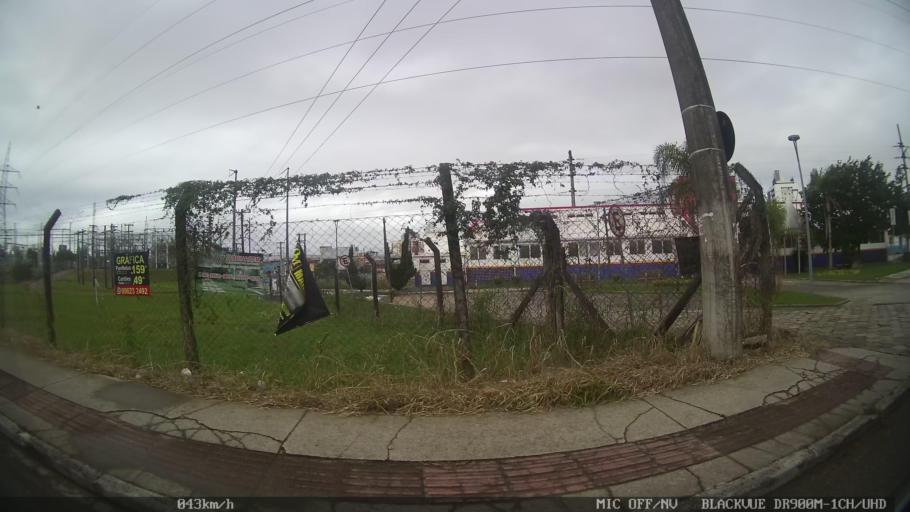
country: BR
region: Santa Catarina
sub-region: Sao Jose
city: Campinas
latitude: -27.5873
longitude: -48.6202
